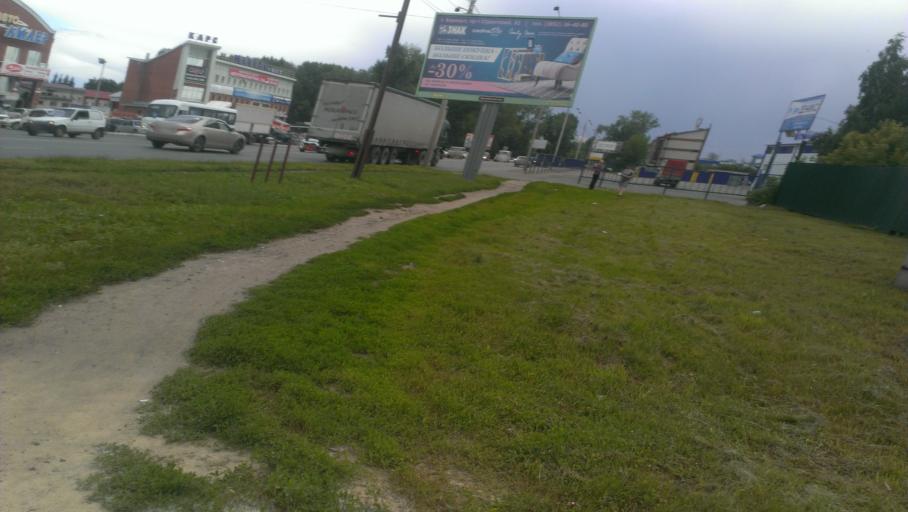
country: RU
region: Altai Krai
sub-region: Gorod Barnaulskiy
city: Barnaul
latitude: 53.3404
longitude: 83.7196
